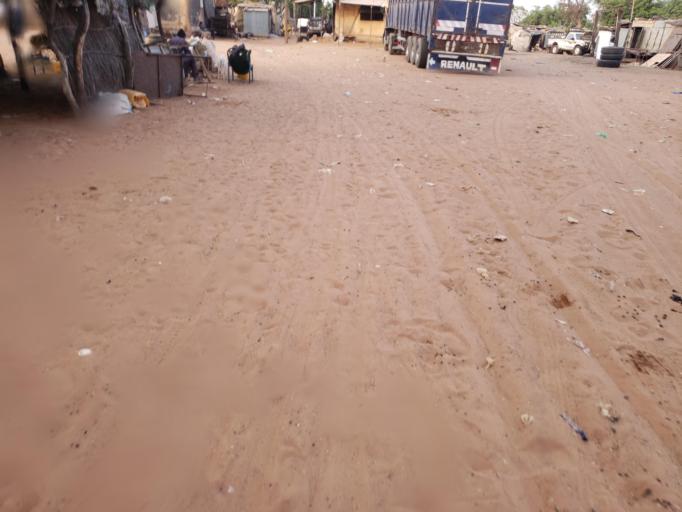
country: SN
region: Louga
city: Ndibene Dahra
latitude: 15.3918
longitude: -15.1136
